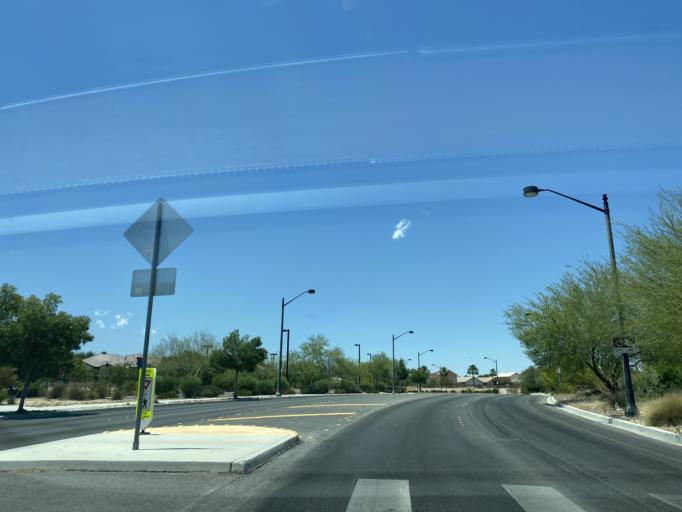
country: US
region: Nevada
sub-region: Clark County
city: Las Vegas
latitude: 36.2831
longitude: -115.2630
